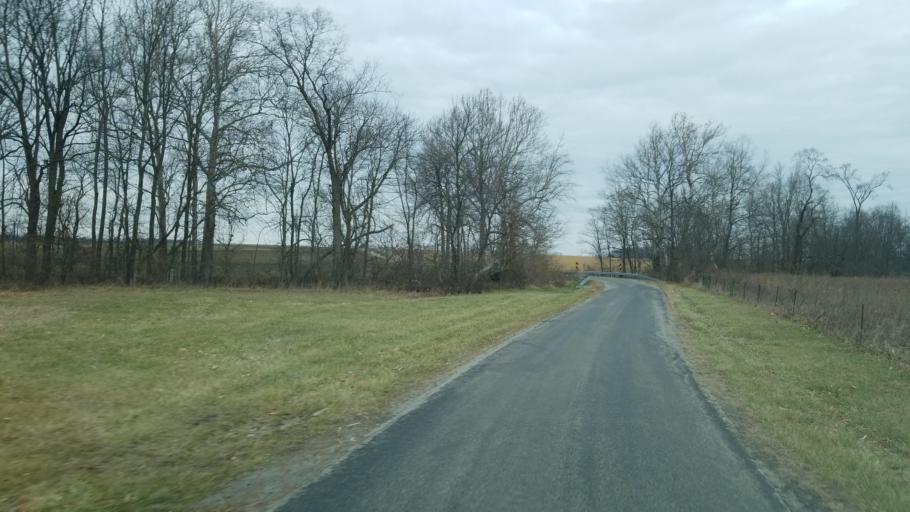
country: US
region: Ohio
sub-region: Highland County
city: Leesburg
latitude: 39.2566
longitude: -83.5277
